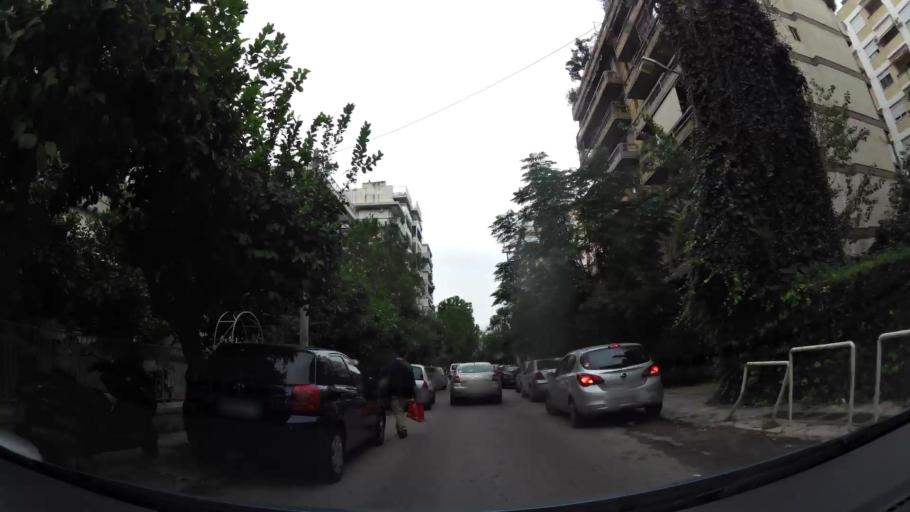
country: GR
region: Attica
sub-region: Nomarchia Athinas
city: Palaio Faliro
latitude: 37.9246
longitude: 23.6975
